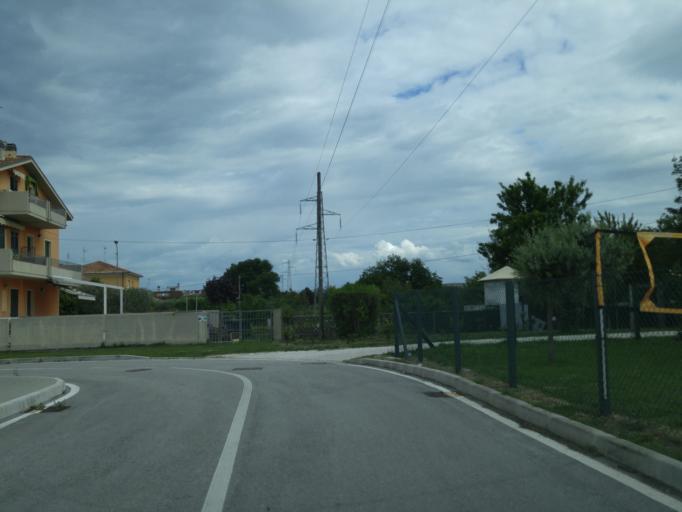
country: IT
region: The Marches
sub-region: Provincia di Pesaro e Urbino
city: Fano
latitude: 43.8325
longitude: 13.0396
